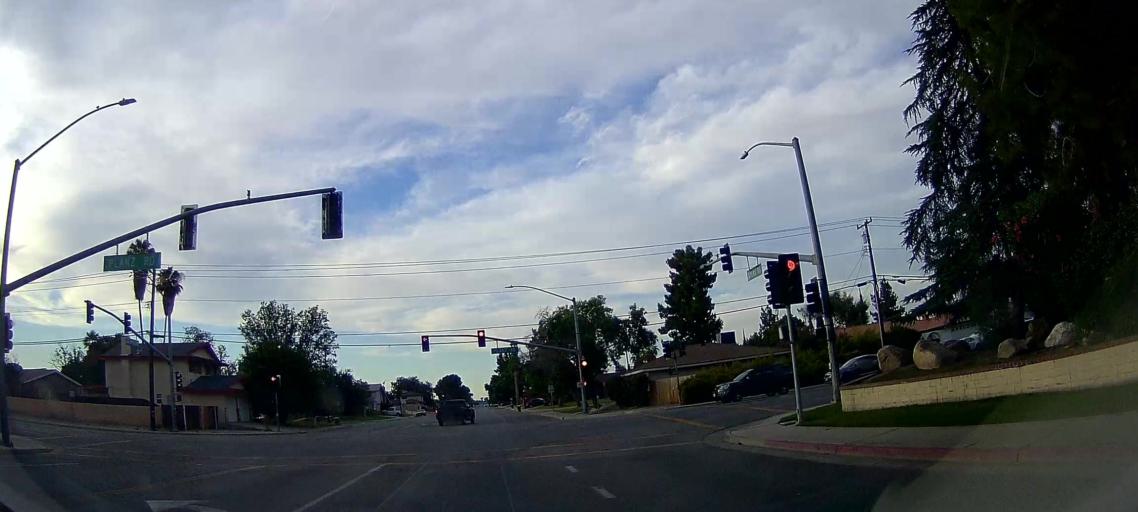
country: US
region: California
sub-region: Kern County
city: Bakersfield
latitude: 35.3248
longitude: -119.0477
